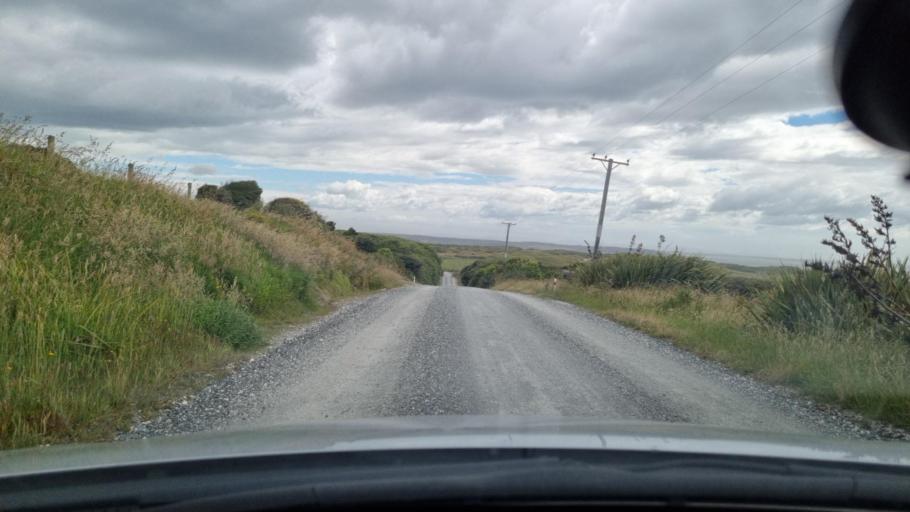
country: NZ
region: Southland
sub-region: Invercargill City
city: Bluff
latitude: -46.5255
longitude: 168.2704
